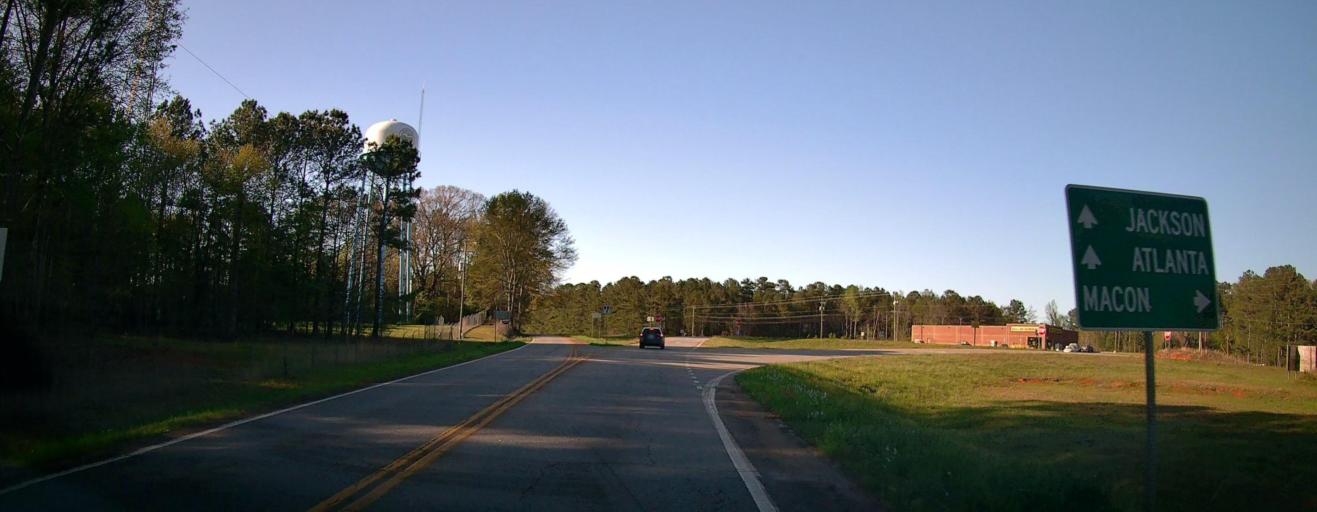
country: US
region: Georgia
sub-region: Butts County
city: Indian Springs
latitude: 33.2629
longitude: -83.9090
